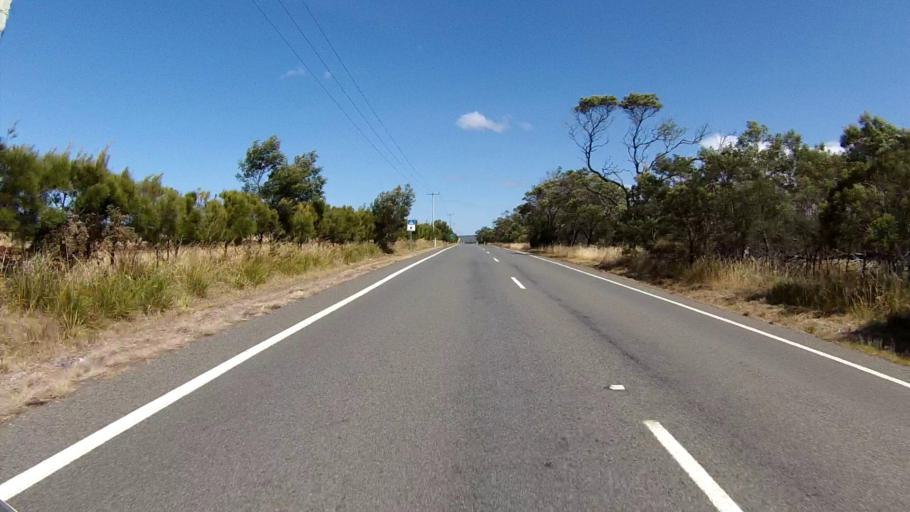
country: AU
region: Tasmania
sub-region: Break O'Day
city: St Helens
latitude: -42.0940
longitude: 148.0648
